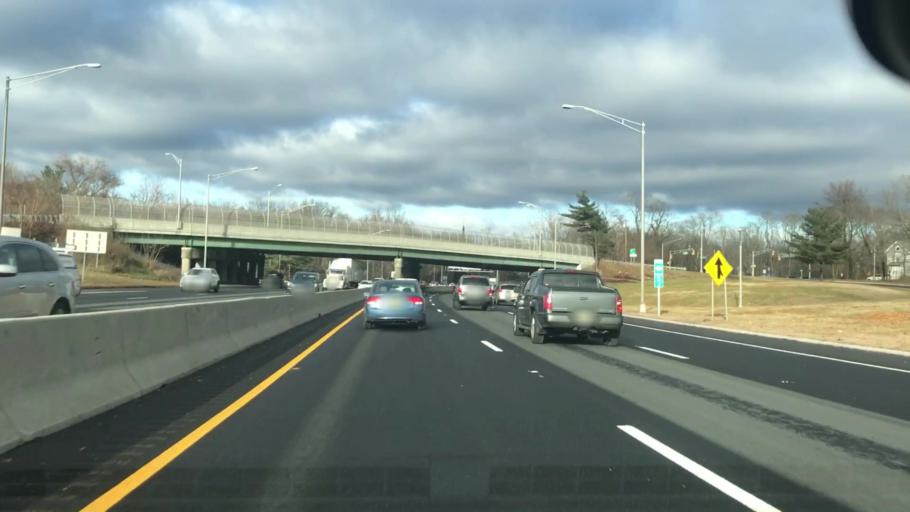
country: US
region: New Jersey
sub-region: Bergen County
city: Ho-Ho-Kus
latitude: 40.9825
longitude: -74.0877
